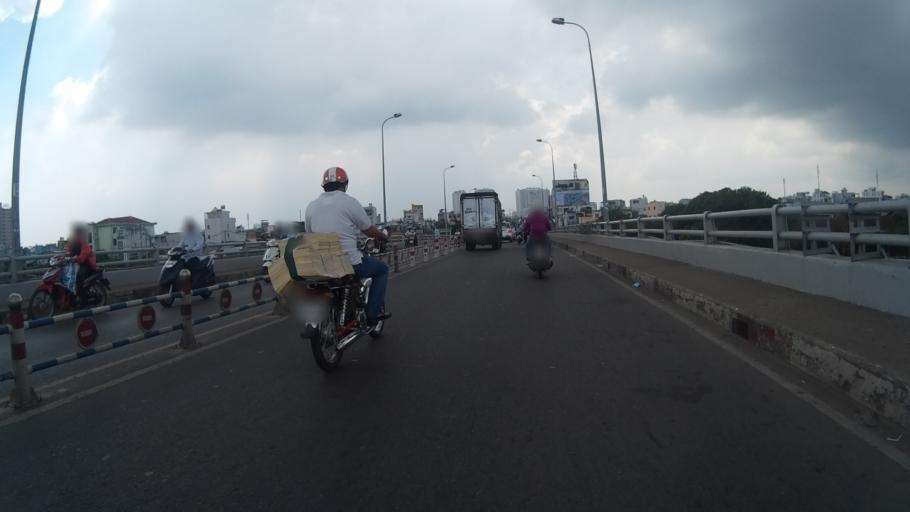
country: VN
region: Ho Chi Minh City
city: Quan Nam
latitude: 10.7498
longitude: 106.6692
